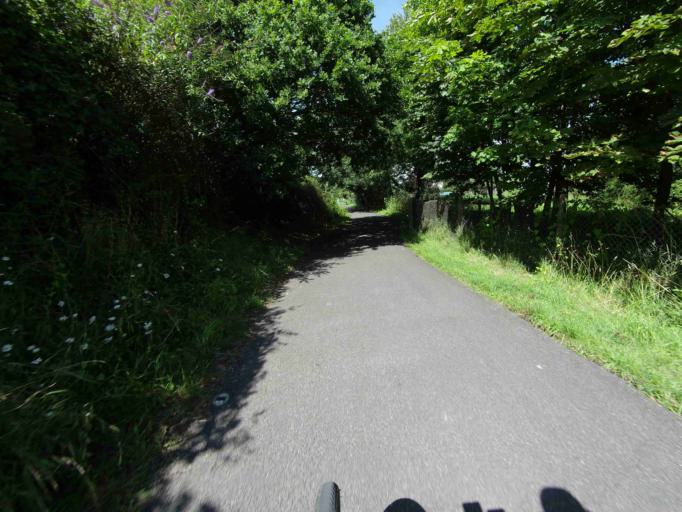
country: GB
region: England
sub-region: Devon
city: Exmouth
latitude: 50.6251
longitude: -3.4152
